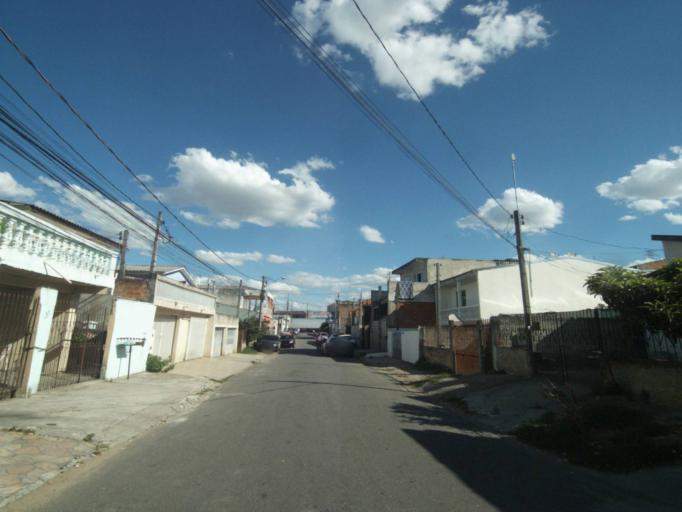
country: BR
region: Parana
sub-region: Curitiba
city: Curitiba
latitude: -25.5130
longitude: -49.3364
